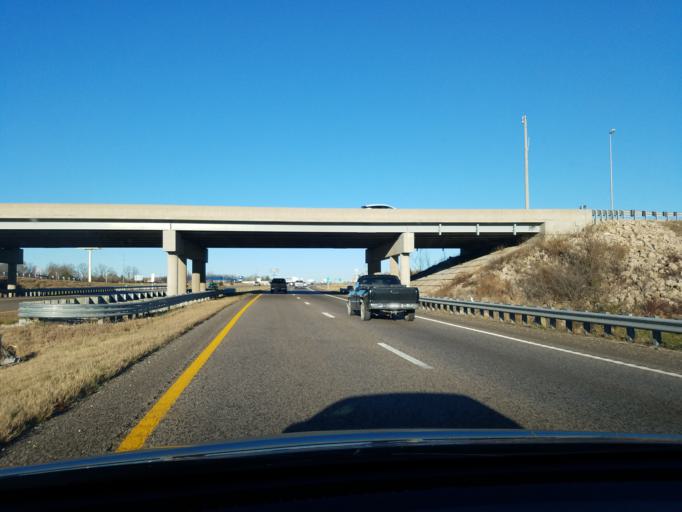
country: US
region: Missouri
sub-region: Franklin County
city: Sullivan
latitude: 38.2115
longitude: -91.1725
